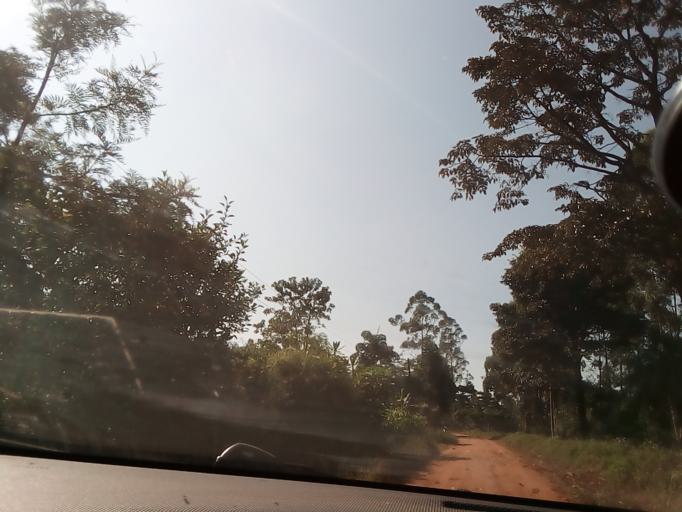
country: UG
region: Central Region
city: Masaka
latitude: -0.3392
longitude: 31.7206
